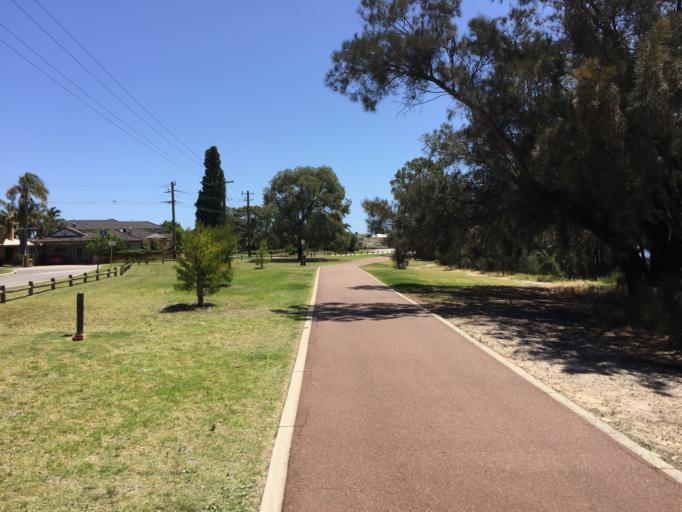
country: AU
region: Western Australia
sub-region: Canning
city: Wilson
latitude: -32.0235
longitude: 115.8981
